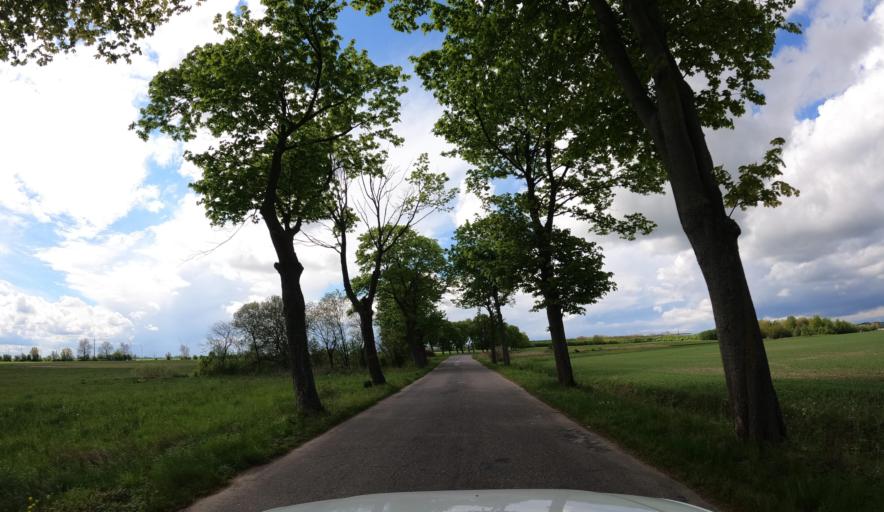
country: PL
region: West Pomeranian Voivodeship
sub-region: Powiat kamienski
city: Wolin
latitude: 53.8630
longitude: 14.6449
